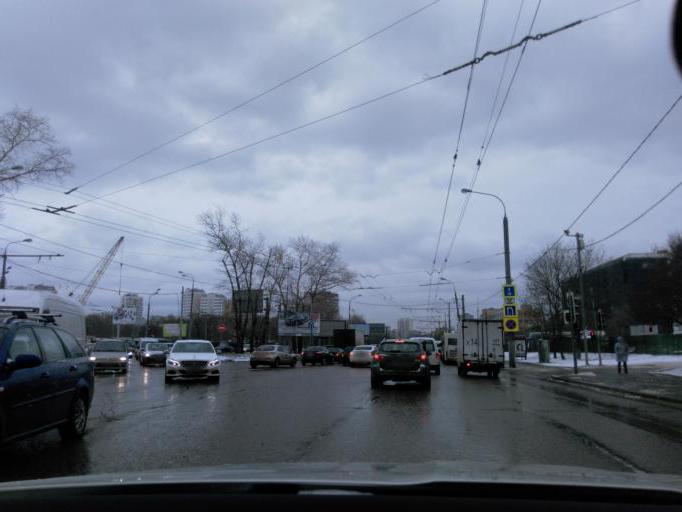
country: RU
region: Moscow
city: Zapadnoye Degunino
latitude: 55.8640
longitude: 37.5475
